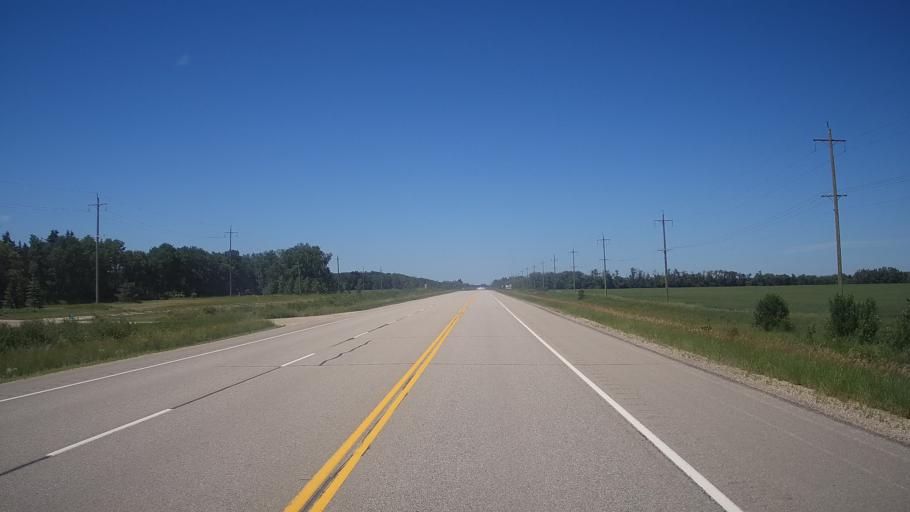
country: CA
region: Manitoba
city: Neepawa
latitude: 50.2253
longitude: -99.3418
